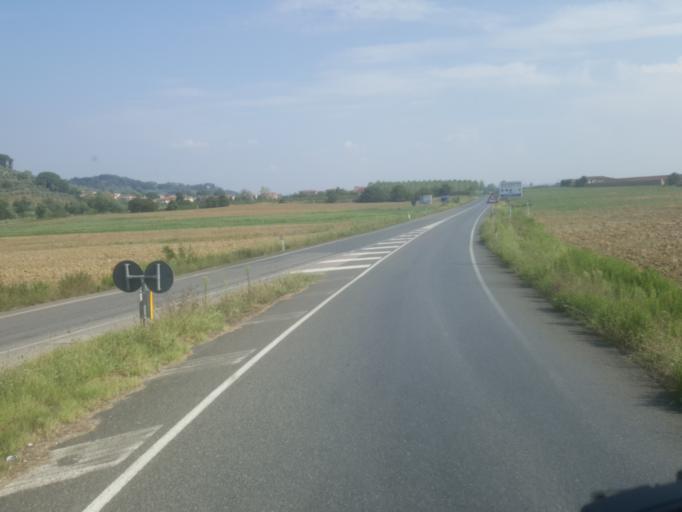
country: IT
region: Tuscany
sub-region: Province of Pisa
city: Treggiaia
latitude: 43.6277
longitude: 10.6601
